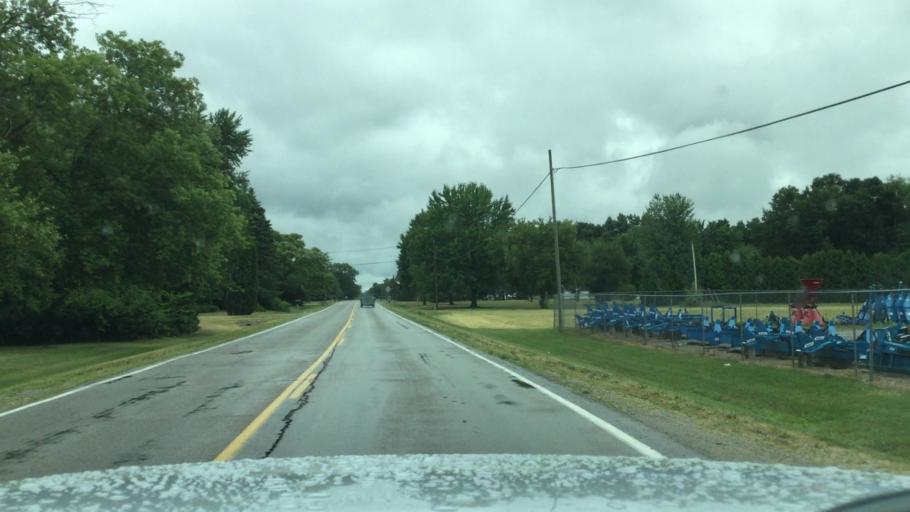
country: US
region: Michigan
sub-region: Genesee County
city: Clio
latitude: 43.1334
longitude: -83.7738
